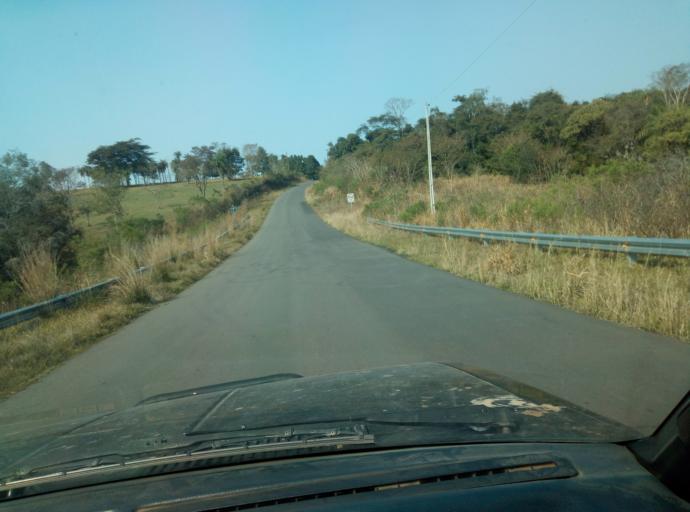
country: PY
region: Caaguazu
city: Carayao
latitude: -25.2422
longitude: -56.2883
